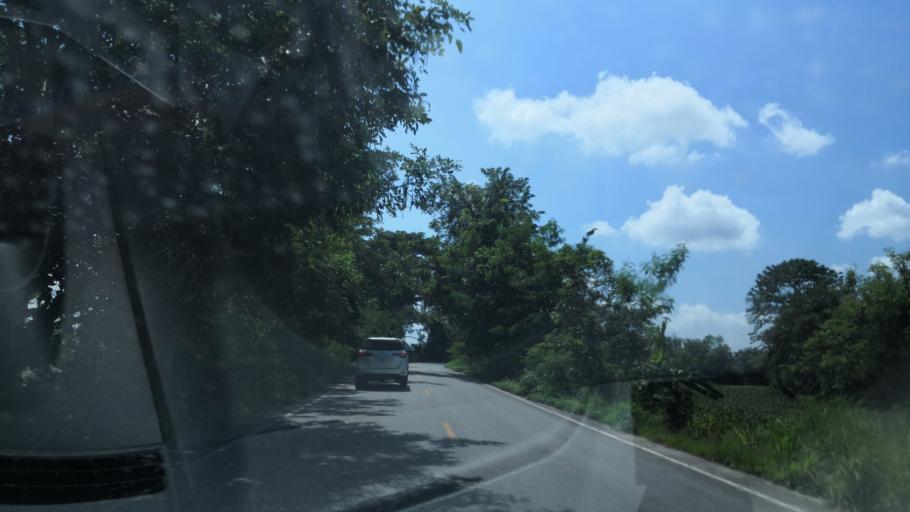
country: TH
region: Chiang Rai
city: Wiang Chai
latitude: 19.9470
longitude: 99.9317
